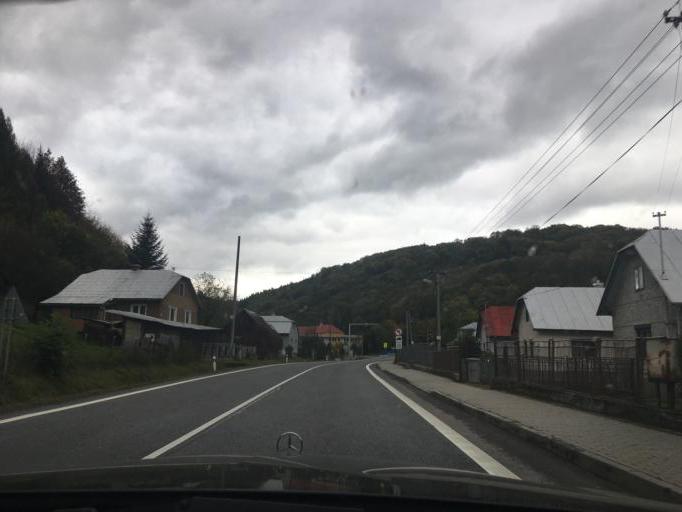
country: SK
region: Presovsky
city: Svidnik
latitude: 49.3634
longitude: 21.6844
